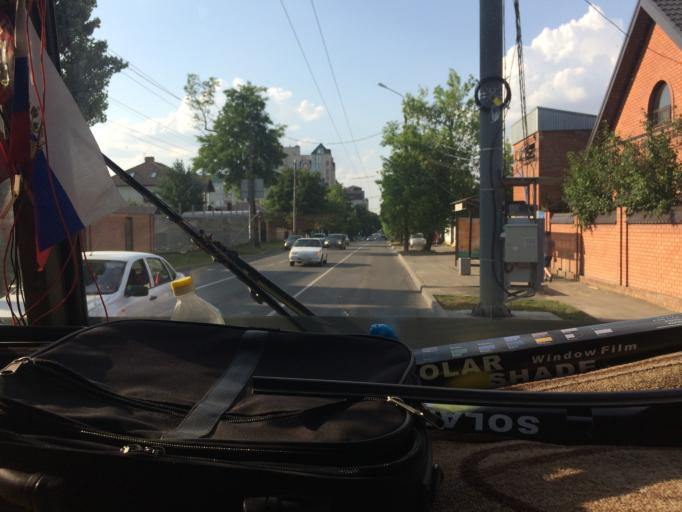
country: RU
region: Stavropol'skiy
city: Stavropol'
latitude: 45.0288
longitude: 41.9533
